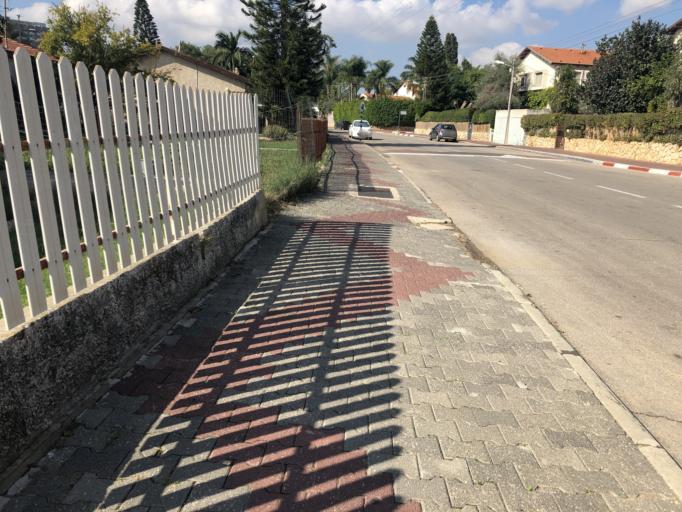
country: IL
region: Tel Aviv
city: Or Yehuda
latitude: 32.0321
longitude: 34.8726
